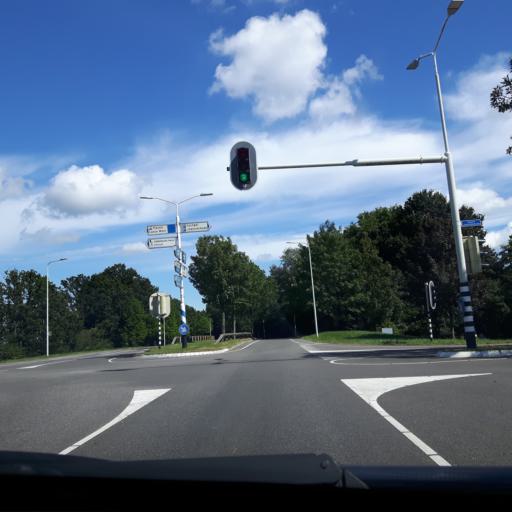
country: NL
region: Zeeland
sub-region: Gemeente Goes
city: Goes
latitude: 51.5093
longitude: 3.8929
